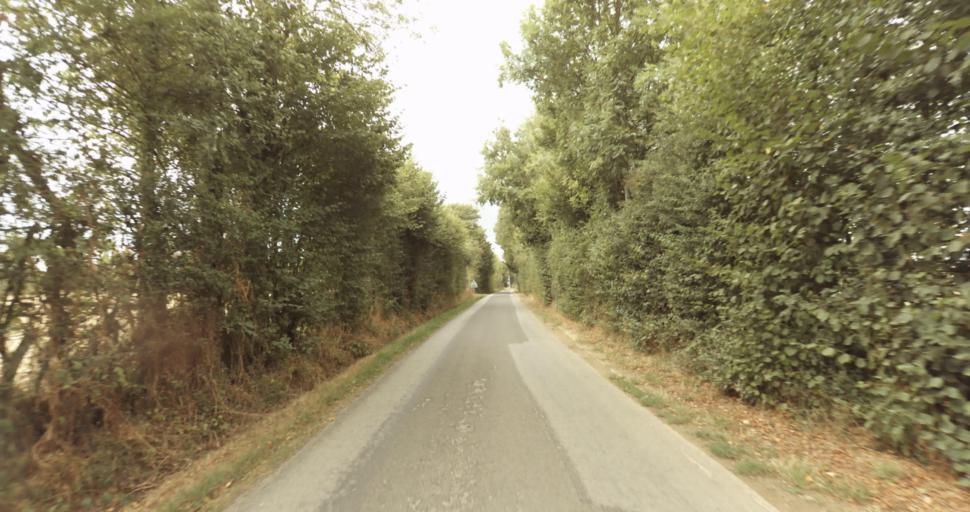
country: FR
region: Lower Normandy
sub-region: Departement du Calvados
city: Orbec
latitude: 48.9065
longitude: 0.3555
